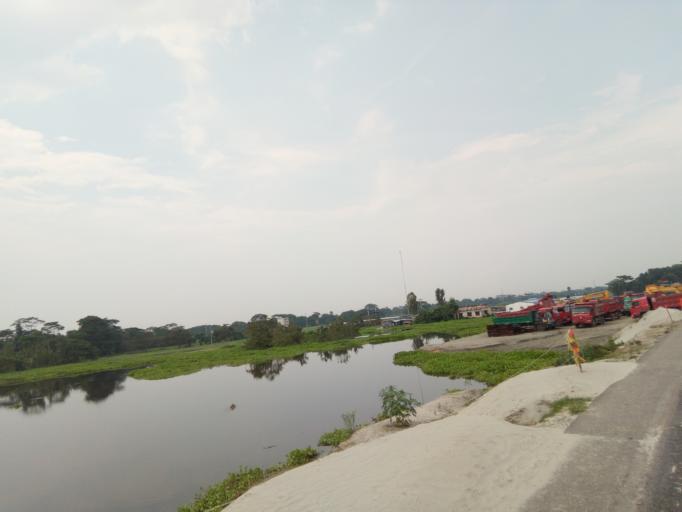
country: BD
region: Dhaka
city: Dohar
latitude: 23.5186
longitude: 90.2799
